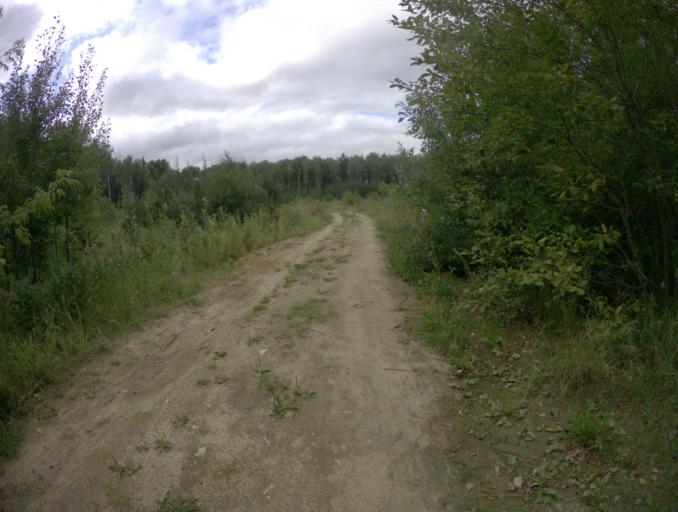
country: RU
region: Vladimir
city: Raduzhnyy
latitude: 56.0070
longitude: 40.3262
